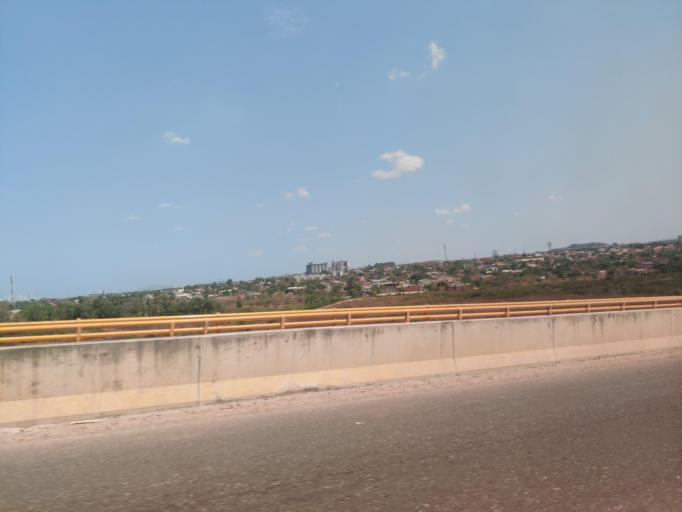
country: CO
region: Bolivar
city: Turbana
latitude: 10.2766
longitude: -75.5182
